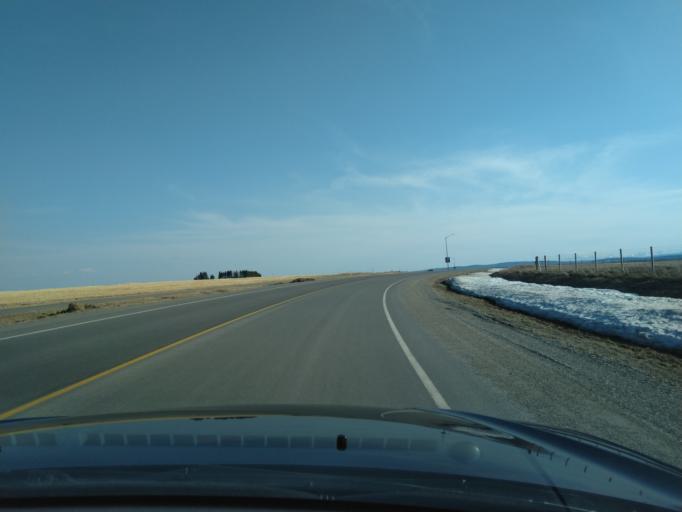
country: CA
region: Alberta
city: Cochrane
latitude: 51.1022
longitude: -114.3881
